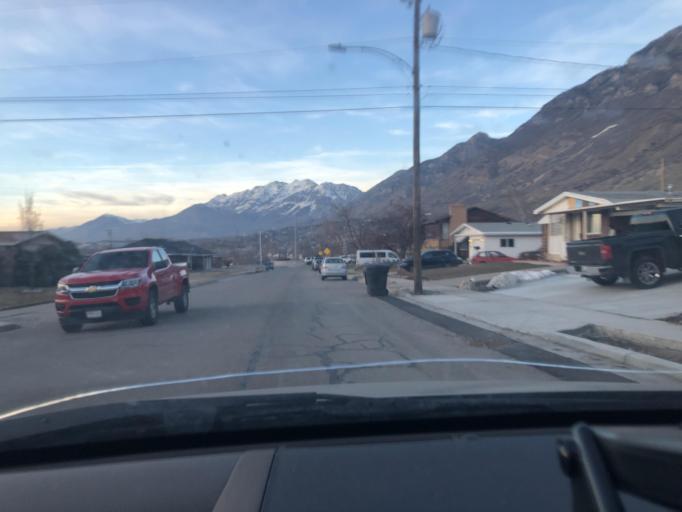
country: US
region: Utah
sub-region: Utah County
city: Provo
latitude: 40.2283
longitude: -111.6352
